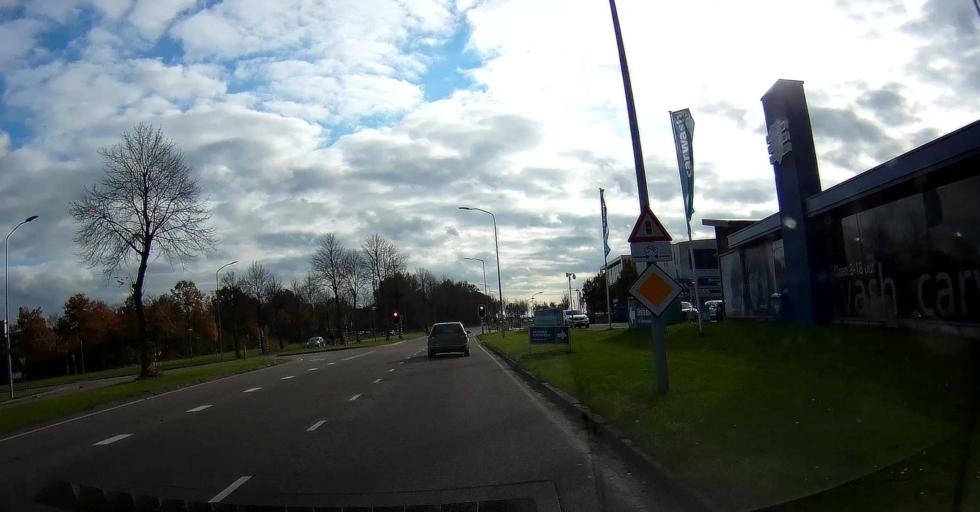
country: NL
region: Flevoland
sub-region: Gemeente Lelystad
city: Lelystad
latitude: 52.4980
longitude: 5.4744
